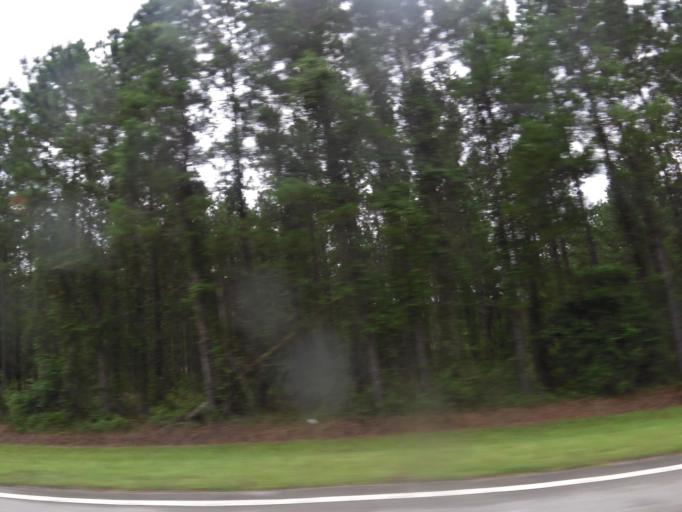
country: US
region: Florida
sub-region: Saint Johns County
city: Saint Augustine South
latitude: 29.8558
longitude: -81.4554
